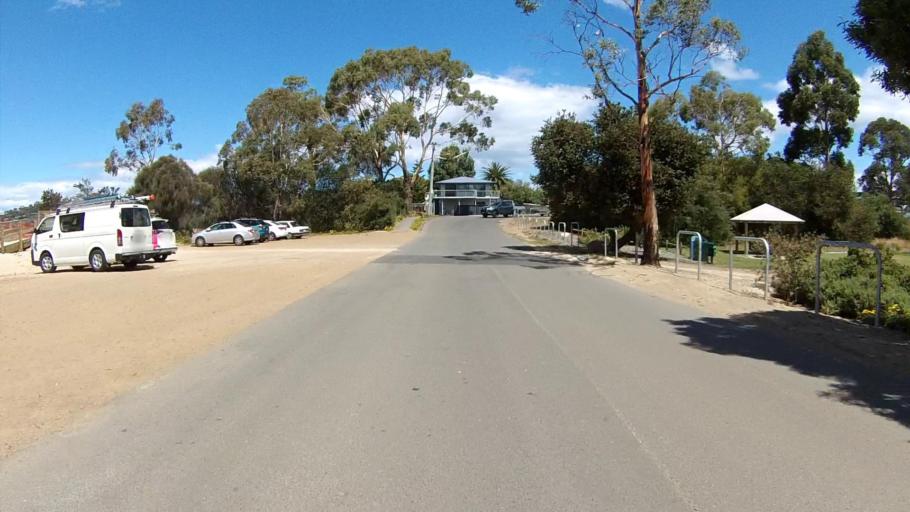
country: AU
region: Tasmania
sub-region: Clarence
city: Lauderdale
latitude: -42.9111
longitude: 147.4951
